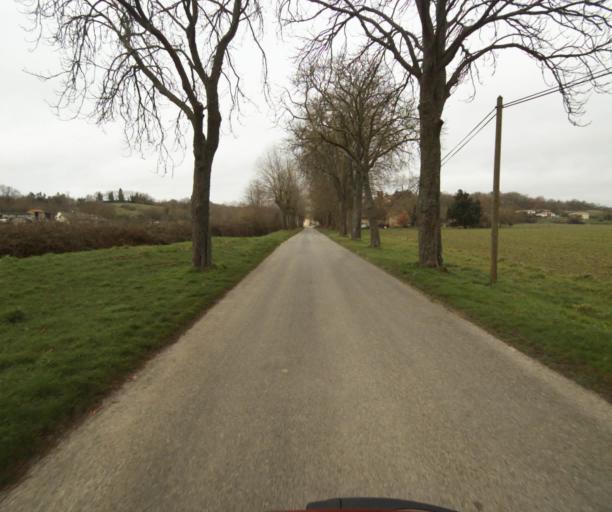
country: FR
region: Midi-Pyrenees
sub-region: Departement de l'Ariege
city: Saverdun
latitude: 43.2552
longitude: 1.5363
